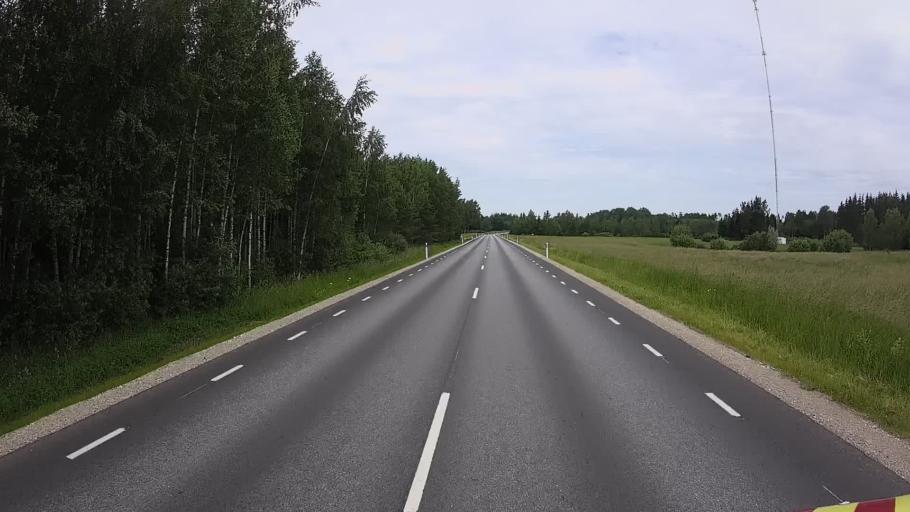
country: EE
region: Viljandimaa
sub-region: Viljandi linn
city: Viljandi
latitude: 58.2339
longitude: 25.5996
